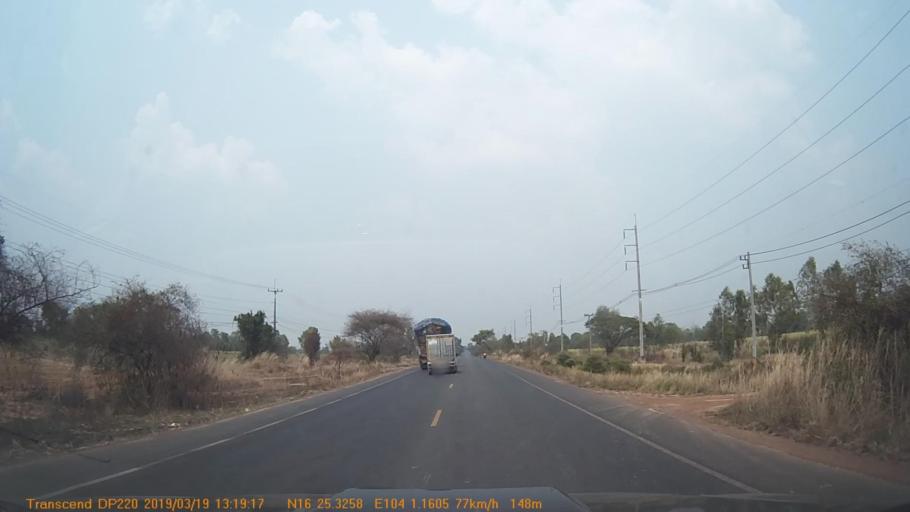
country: TH
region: Kalasin
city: Kuchinarai
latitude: 16.4225
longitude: 104.0195
